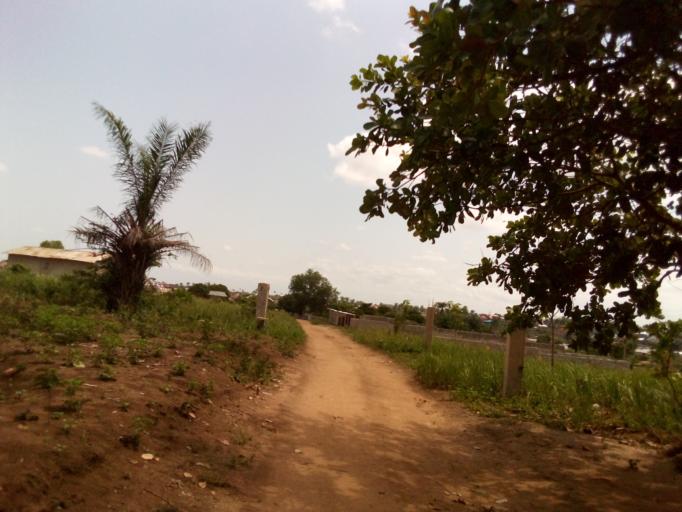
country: SL
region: Western Area
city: Waterloo
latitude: 8.3412
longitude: -13.0238
